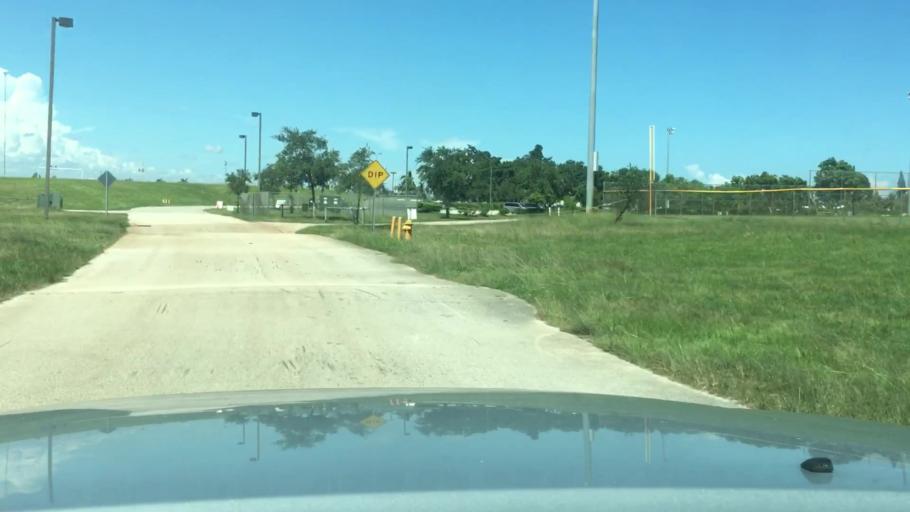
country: US
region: Florida
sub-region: Miami-Dade County
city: Ives Estates
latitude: 25.9703
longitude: -80.1685
